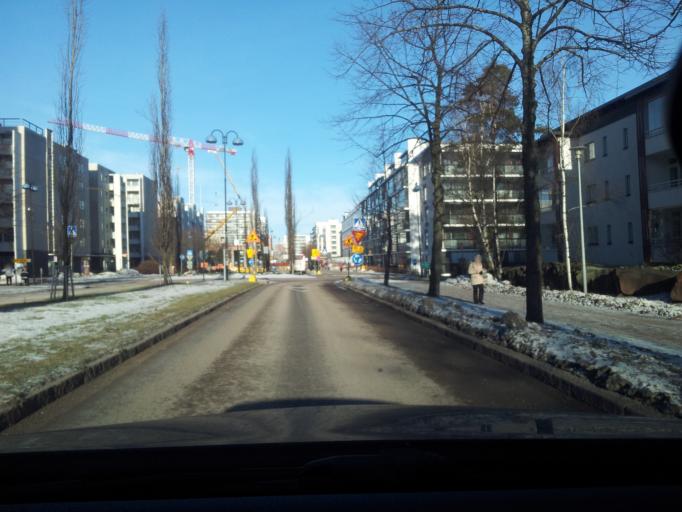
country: FI
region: Uusimaa
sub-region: Helsinki
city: Koukkuniemi
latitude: 60.1580
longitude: 24.7429
